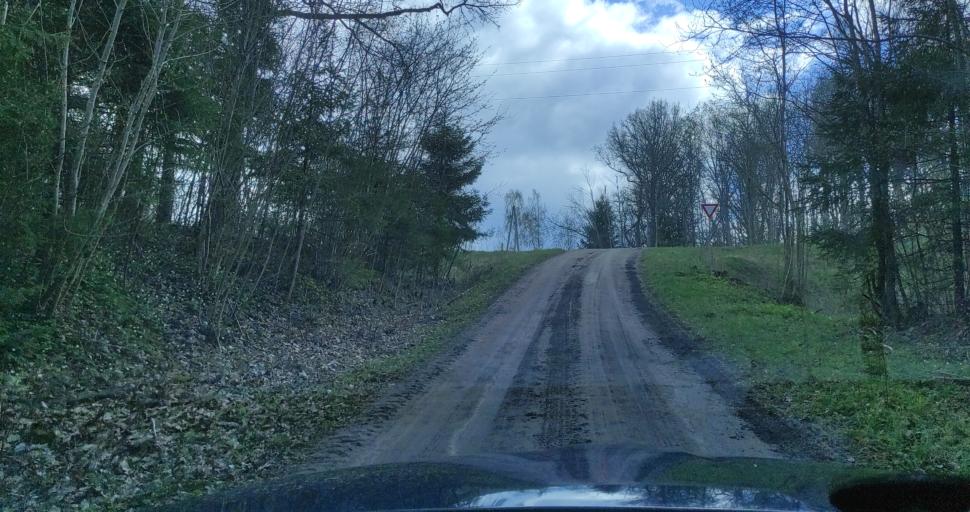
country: LV
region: Kuldigas Rajons
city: Kuldiga
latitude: 56.8619
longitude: 21.8316
